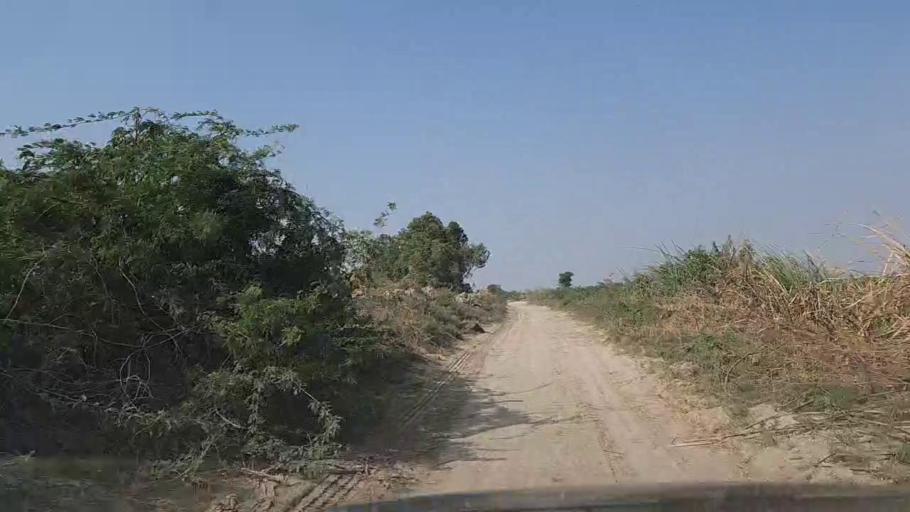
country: PK
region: Sindh
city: Gharo
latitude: 24.7281
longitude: 67.7036
